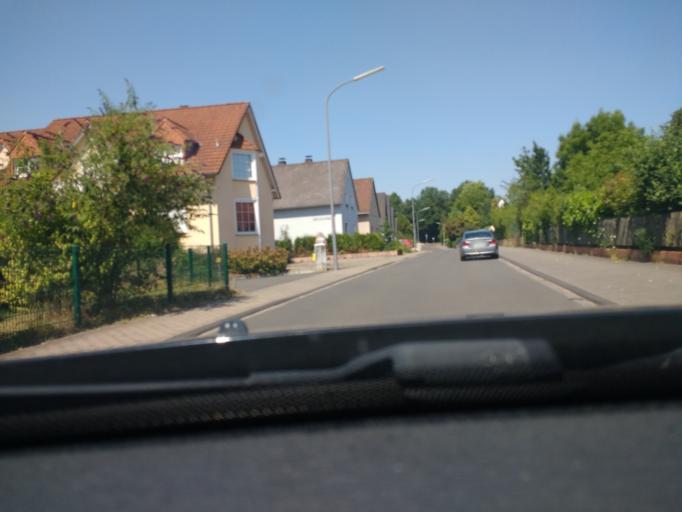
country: DE
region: Rheinland-Pfalz
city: Wittlich
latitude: 49.9948
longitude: 6.8842
